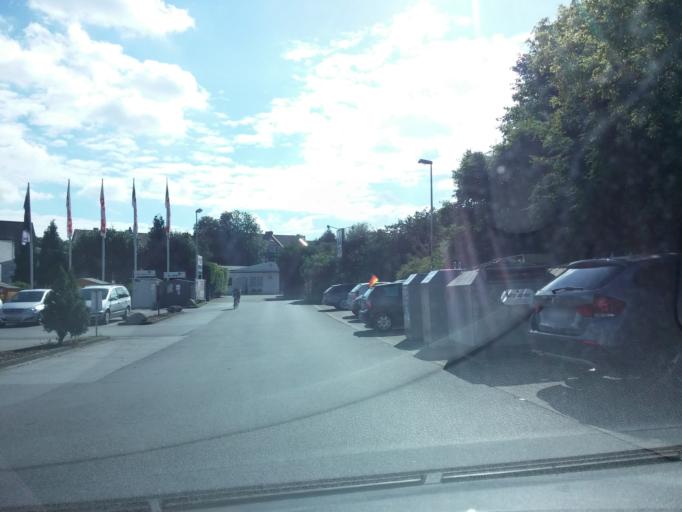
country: DE
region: North Rhine-Westphalia
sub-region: Regierungsbezirk Munster
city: Gladbeck
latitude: 51.5856
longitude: 7.0355
